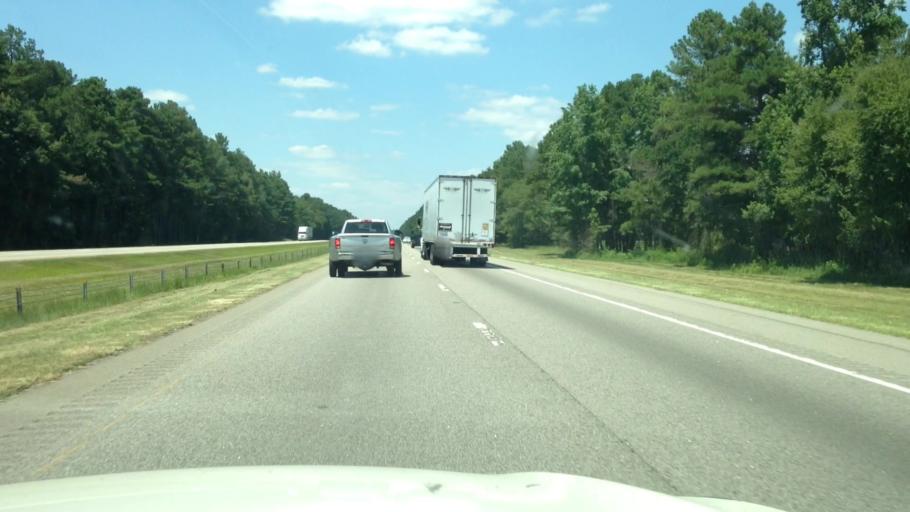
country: US
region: North Carolina
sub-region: Robeson County
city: Saint Pauls
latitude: 34.7726
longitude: -78.9959
